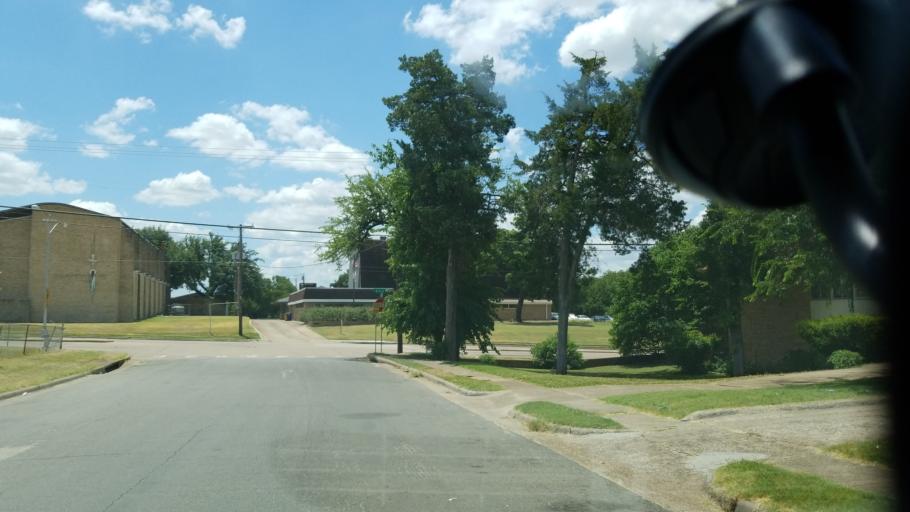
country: US
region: Texas
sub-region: Dallas County
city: Cockrell Hill
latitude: 32.7064
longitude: -96.8432
